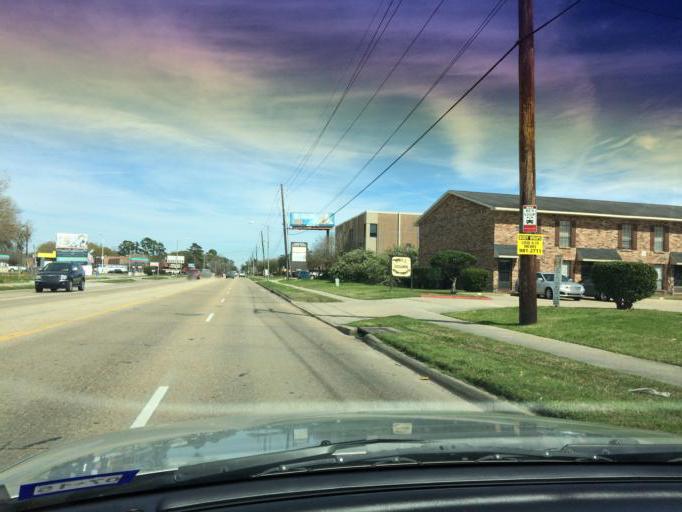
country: US
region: Louisiana
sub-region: Lafayette Parish
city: Scott
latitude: 30.1991
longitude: -92.0687
